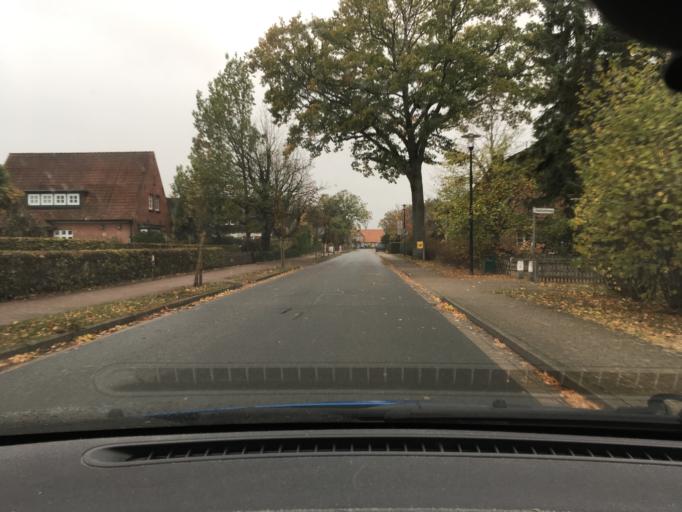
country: DE
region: Lower Saxony
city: Radbruch
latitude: 53.3130
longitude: 10.2872
